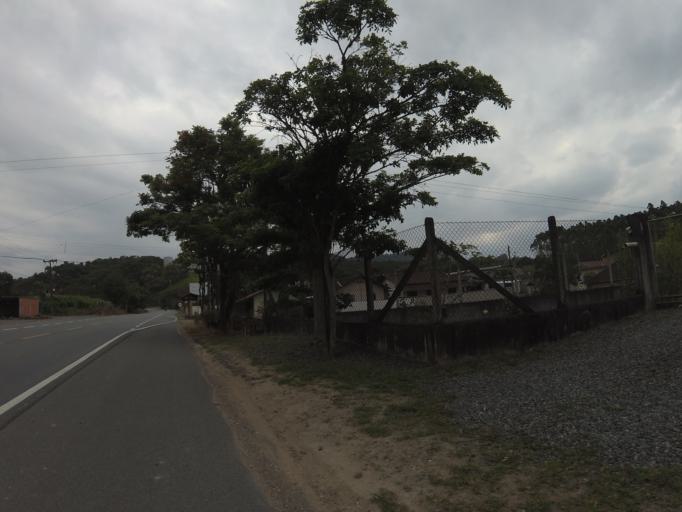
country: BR
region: Santa Catarina
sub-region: Indaial
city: Indaial
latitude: -26.8340
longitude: -49.1638
